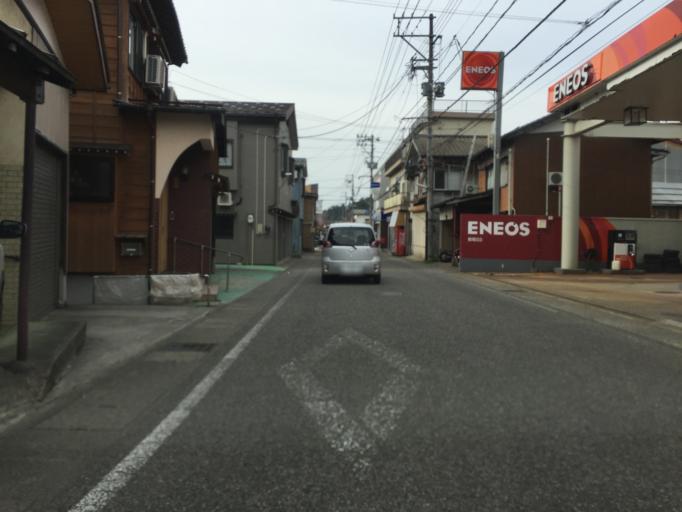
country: JP
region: Niigata
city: Tochio-honcho
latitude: 37.4682
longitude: 139.0035
